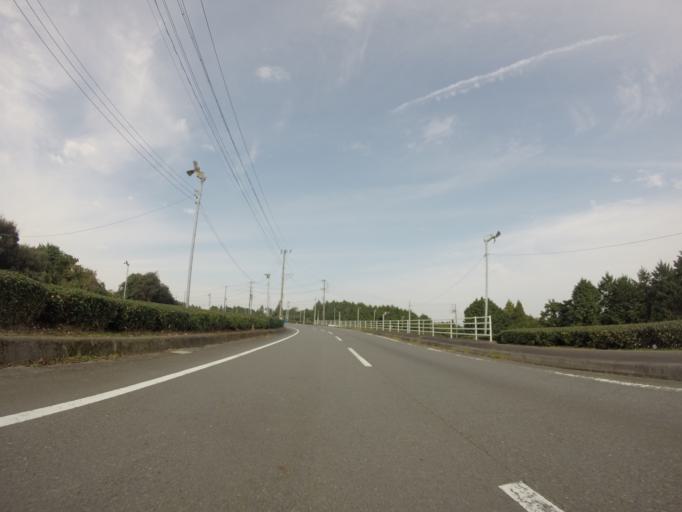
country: JP
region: Shizuoka
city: Shimada
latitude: 34.7721
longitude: 138.1637
